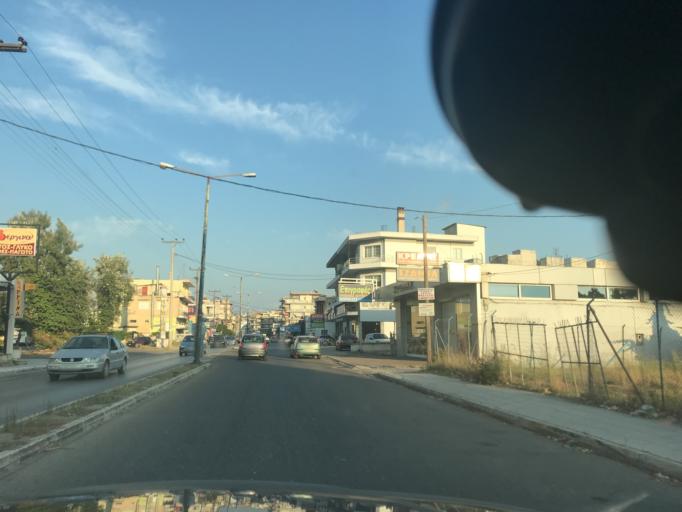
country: GR
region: West Greece
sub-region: Nomos Ileias
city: Pyrgos
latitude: 37.6772
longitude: 21.4294
